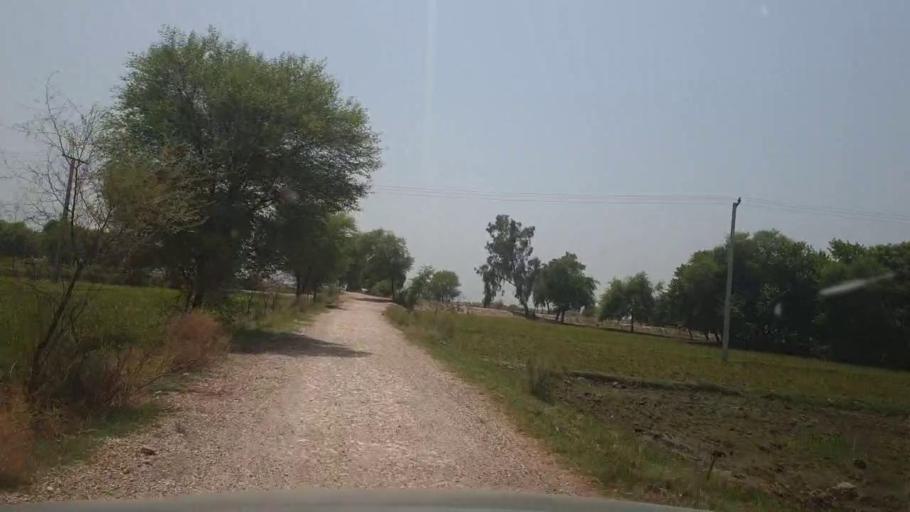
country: PK
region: Sindh
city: Lakhi
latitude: 27.8460
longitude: 68.6641
